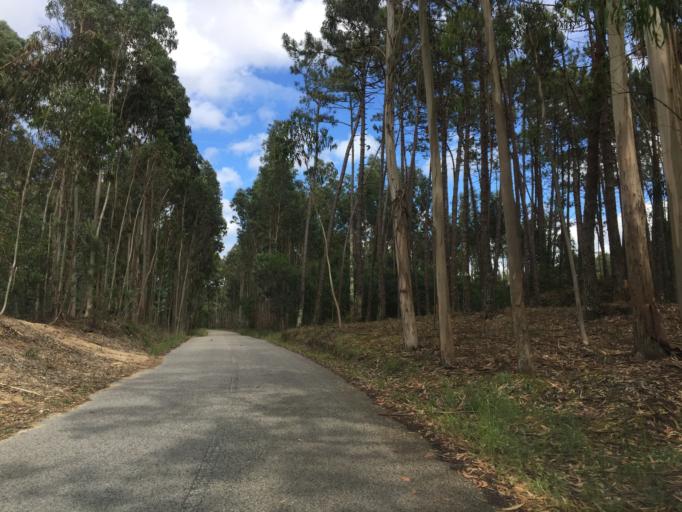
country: PT
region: Coimbra
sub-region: Figueira da Foz
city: Tavarede
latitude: 40.2109
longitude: -8.8398
